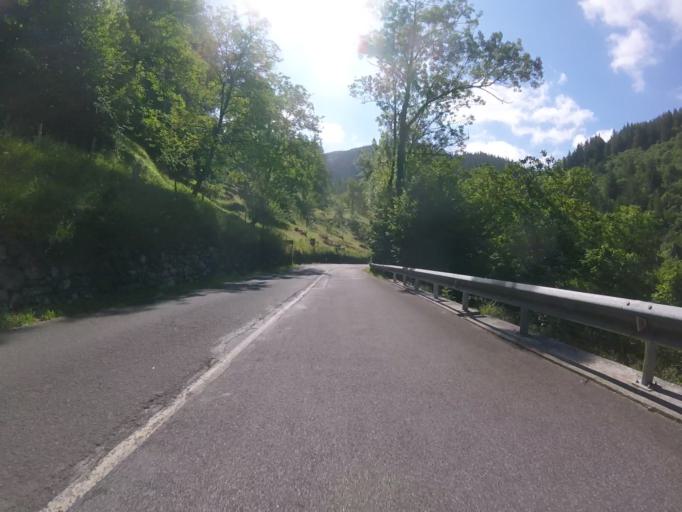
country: ES
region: Basque Country
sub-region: Provincia de Guipuzcoa
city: Beizama
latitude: 43.0982
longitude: -2.2395
